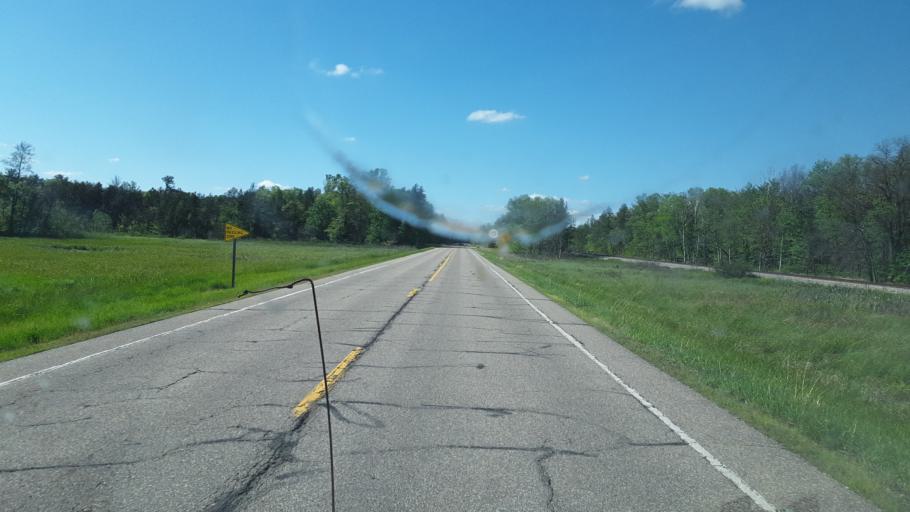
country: US
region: Wisconsin
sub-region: Juneau County
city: New Lisbon
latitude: 44.1314
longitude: -90.1259
